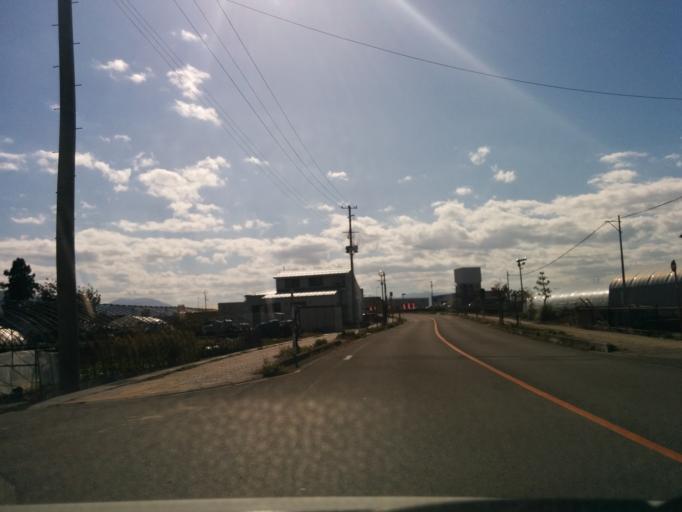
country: JP
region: Fukushima
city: Kitakata
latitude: 37.5202
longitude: 139.9339
